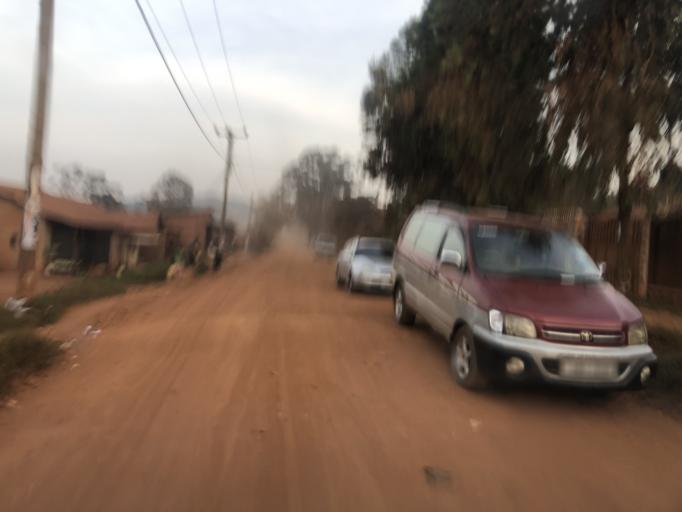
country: UG
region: Central Region
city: Kampala Central Division
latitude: 0.2982
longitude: 32.5185
